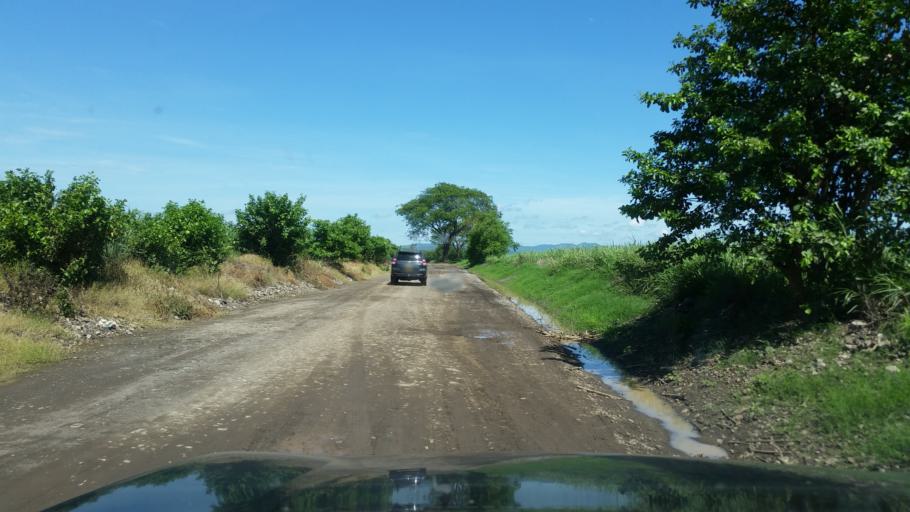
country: NI
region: Chinandega
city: Puerto Morazan
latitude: 12.7741
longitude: -87.1026
